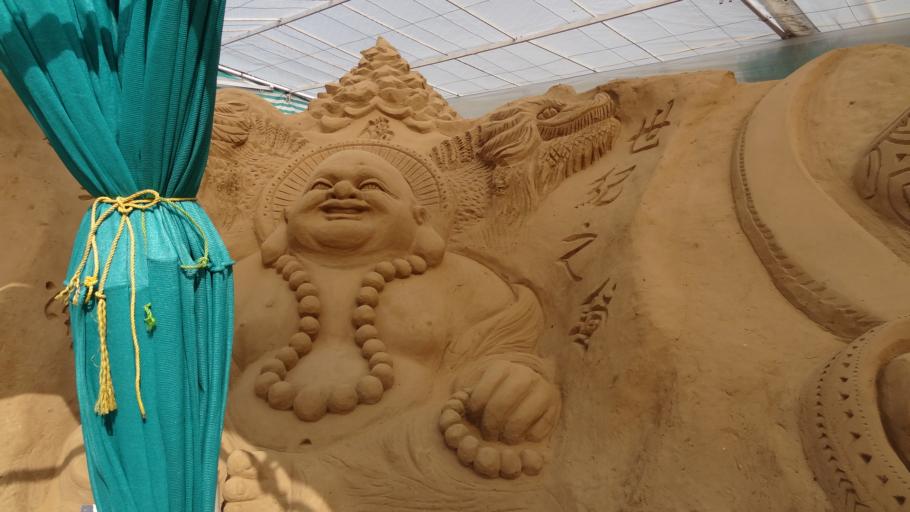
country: IN
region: Karnataka
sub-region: Mysore
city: Mysore
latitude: 12.2949
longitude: 76.6820
